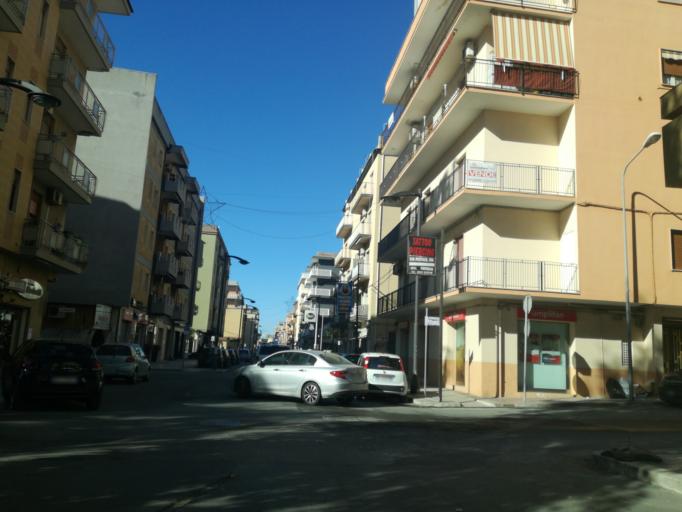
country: IT
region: Sicily
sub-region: Provincia di Caltanissetta
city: Gela
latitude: 37.0731
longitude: 14.2338
